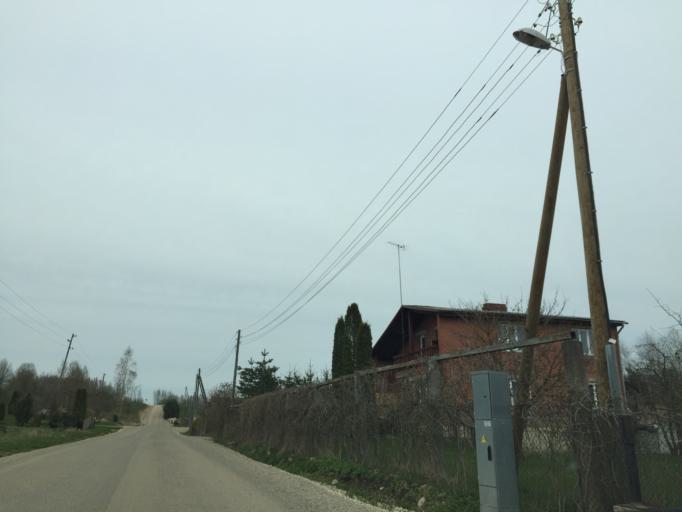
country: LV
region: Ludzas Rajons
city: Ludza
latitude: 56.5498
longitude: 27.6972
